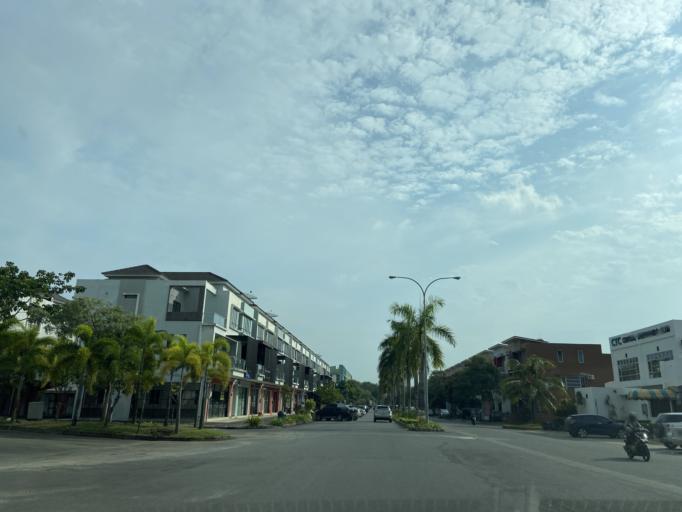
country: SG
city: Singapore
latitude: 1.1002
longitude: 104.0337
